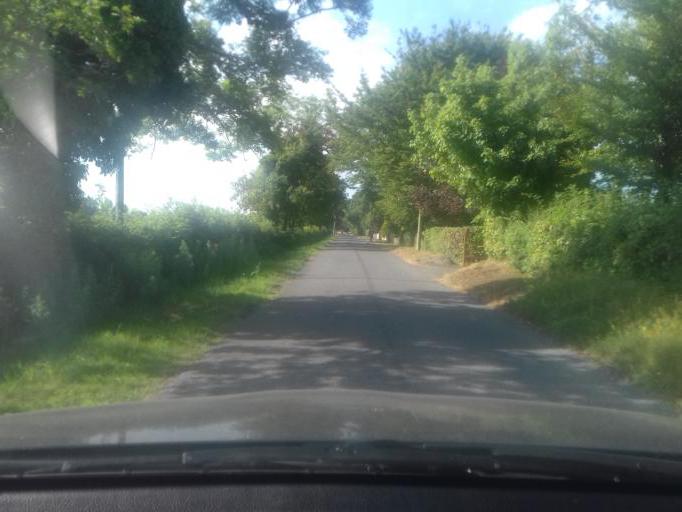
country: IE
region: Leinster
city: Hartstown
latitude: 53.4322
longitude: -6.4279
